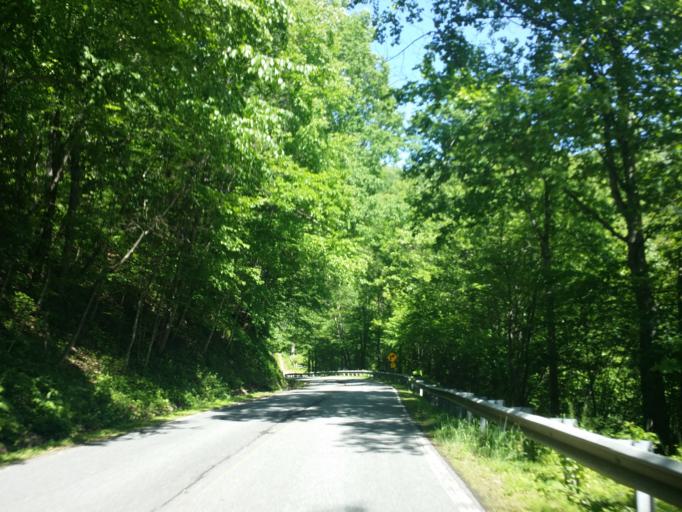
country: US
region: North Carolina
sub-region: Madison County
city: Marshall
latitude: 35.7058
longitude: -82.8251
